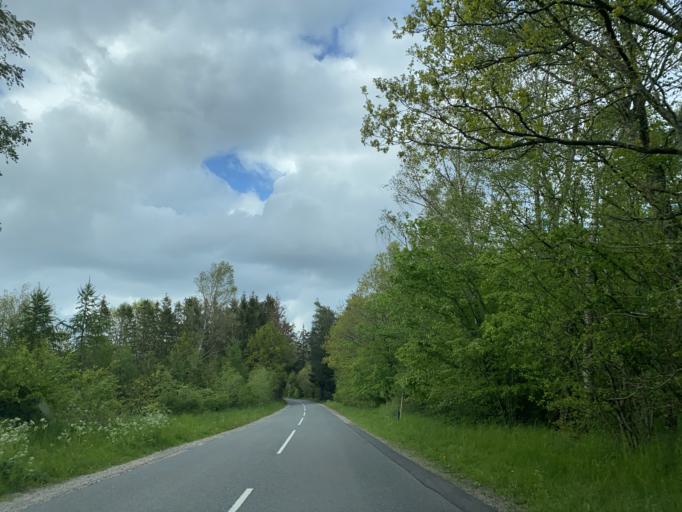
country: DK
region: Central Jutland
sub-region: Horsens Kommune
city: Braedstrup
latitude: 56.0298
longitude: 9.6544
